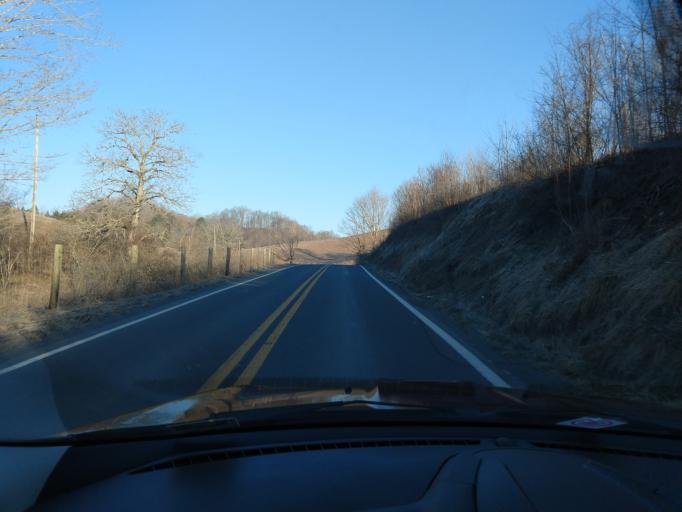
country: US
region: West Virginia
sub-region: Greenbrier County
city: Rainelle
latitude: 37.8687
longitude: -80.7245
